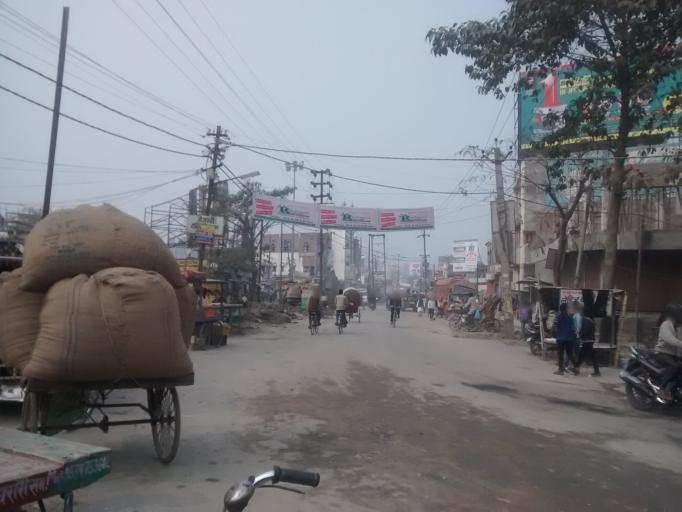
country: IN
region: Bihar
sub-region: Muzaffarpur
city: Muzaffarpur
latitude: 26.1036
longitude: 85.3996
